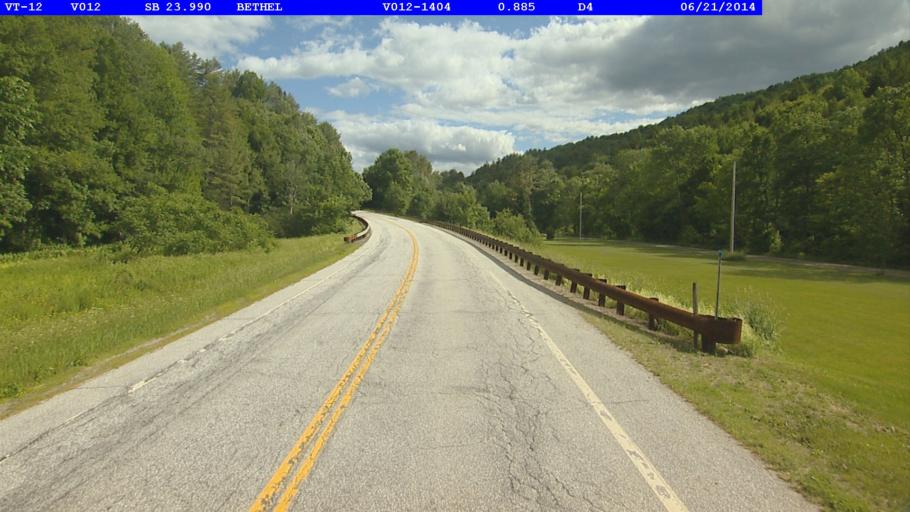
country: US
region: Vermont
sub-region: Orange County
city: Randolph
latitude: 43.8030
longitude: -72.6532
